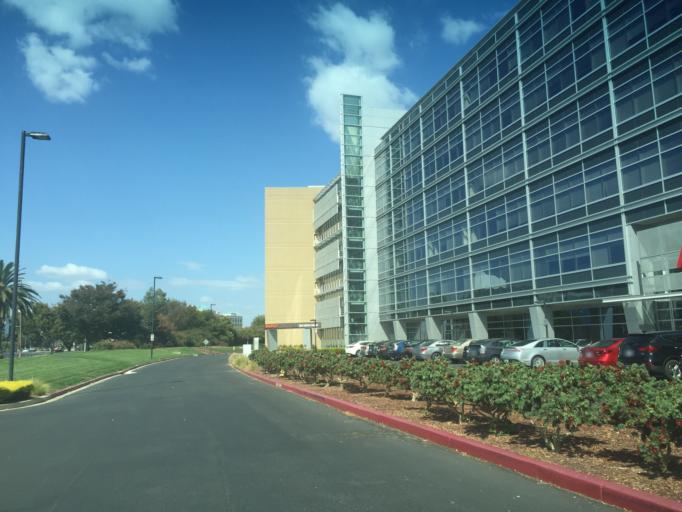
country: US
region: California
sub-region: Santa Clara County
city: Santa Clara
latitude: 37.3979
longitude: -121.9775
